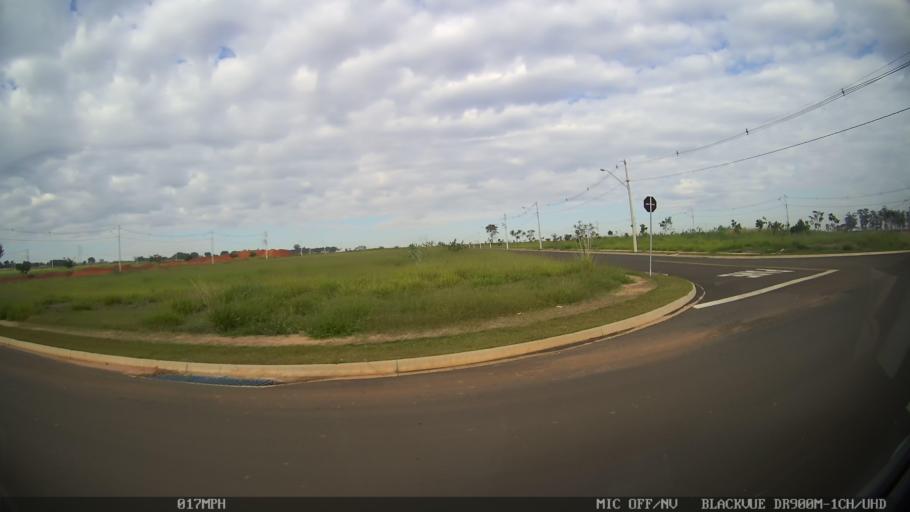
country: BR
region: Sao Paulo
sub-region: Americana
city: Americana
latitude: -22.7115
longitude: -47.3751
